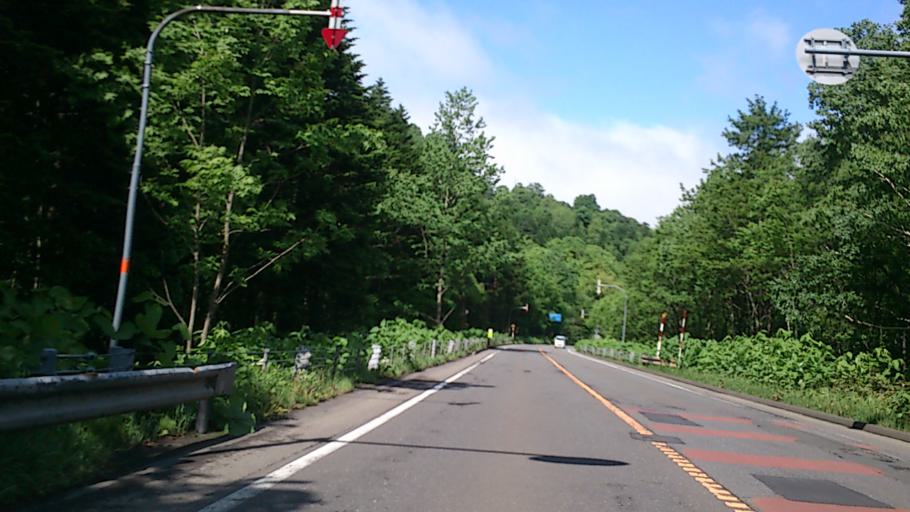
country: JP
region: Hokkaido
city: Shiraoi
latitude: 42.7188
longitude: 141.2140
